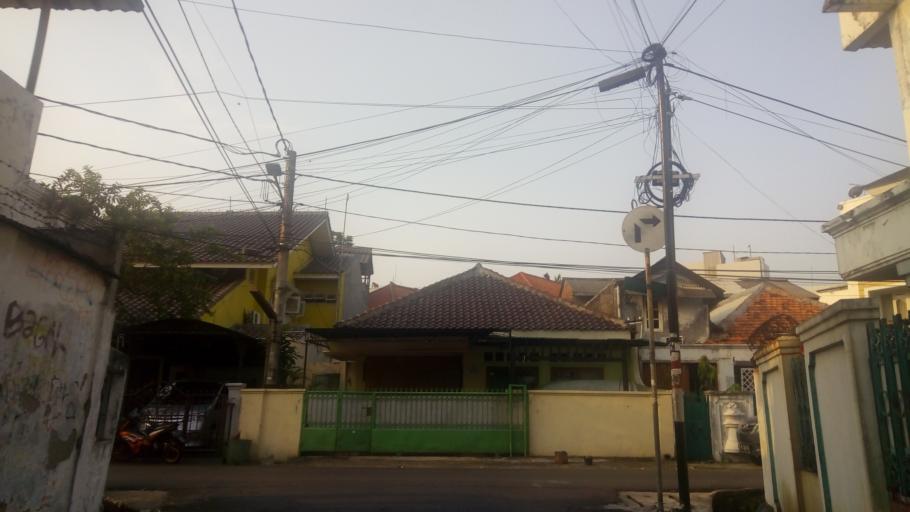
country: ID
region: Jakarta Raya
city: Jakarta
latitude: -6.2038
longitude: 106.8549
